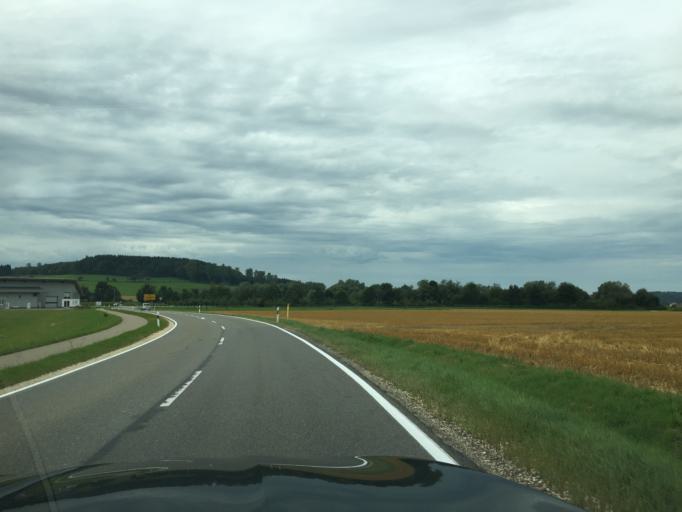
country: DE
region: Baden-Wuerttemberg
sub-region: Tuebingen Region
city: Rot
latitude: 47.8814
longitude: 9.1277
